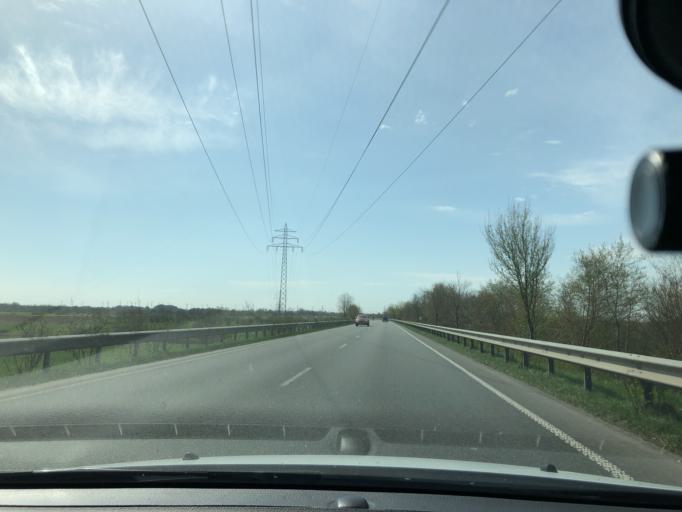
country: DE
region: Schleswig-Holstein
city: Jarplund-Weding
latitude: 54.7316
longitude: 9.3788
